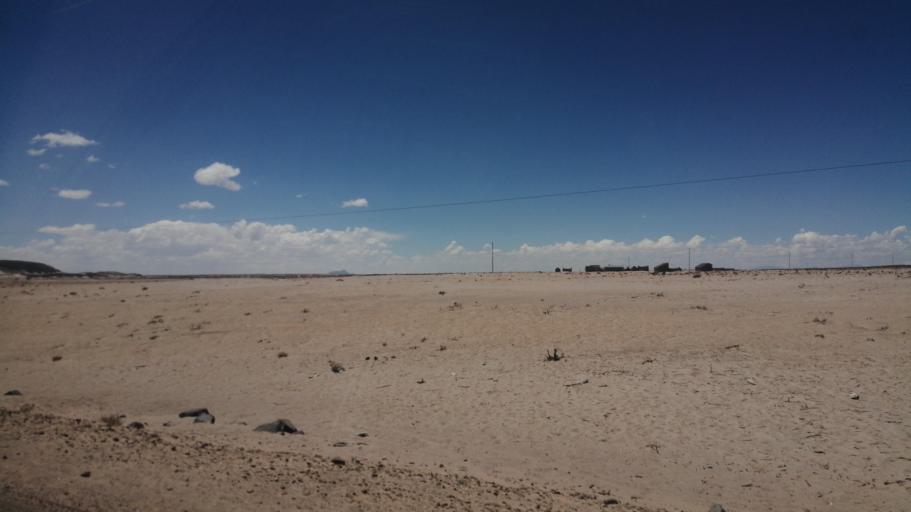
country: BO
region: Oruro
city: Challapata
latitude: -19.2142
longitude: -67.0211
